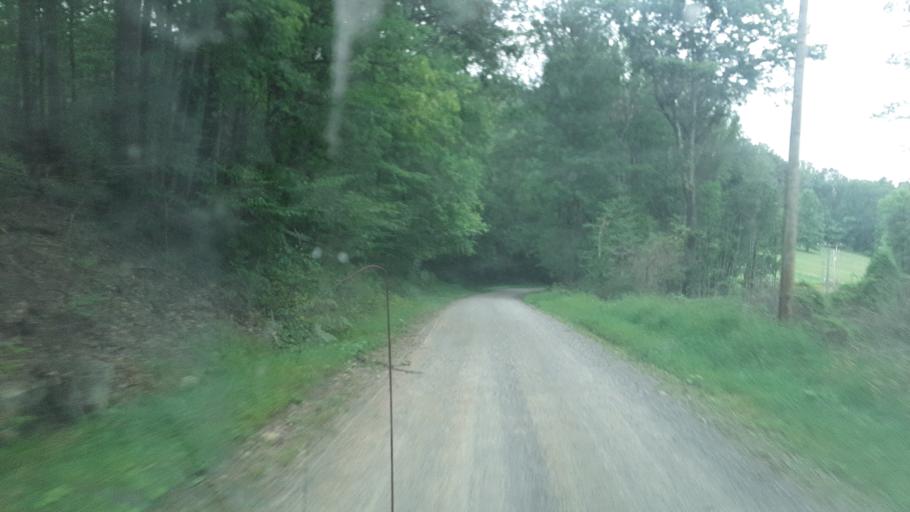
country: US
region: Pennsylvania
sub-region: Jefferson County
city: Punxsutawney
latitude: 40.9512
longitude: -79.1514
